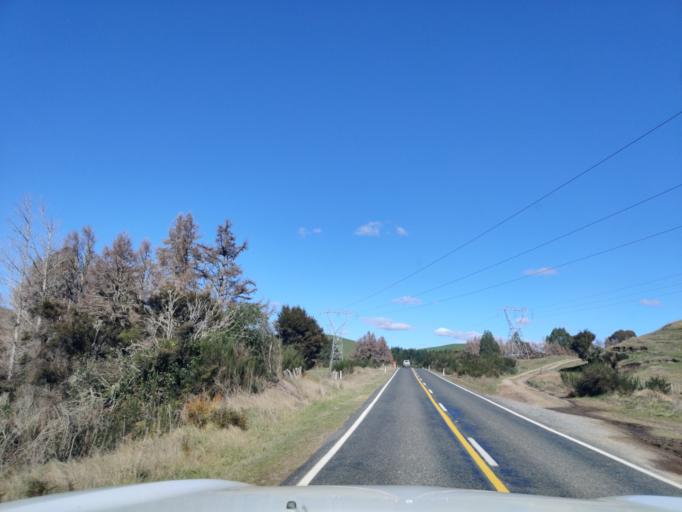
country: NZ
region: Waikato
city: Turangi
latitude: -38.8459
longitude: 175.6843
